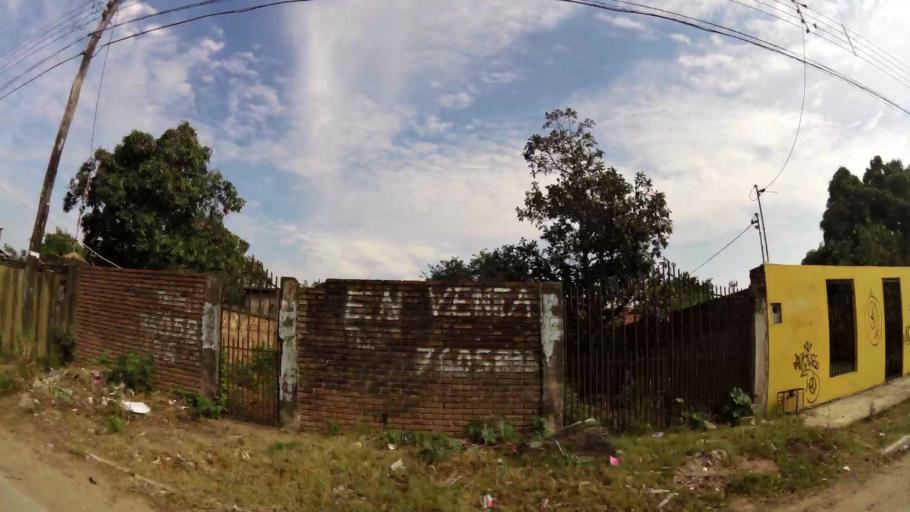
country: BO
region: Santa Cruz
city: Santa Cruz de la Sierra
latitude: -17.7352
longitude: -63.1377
